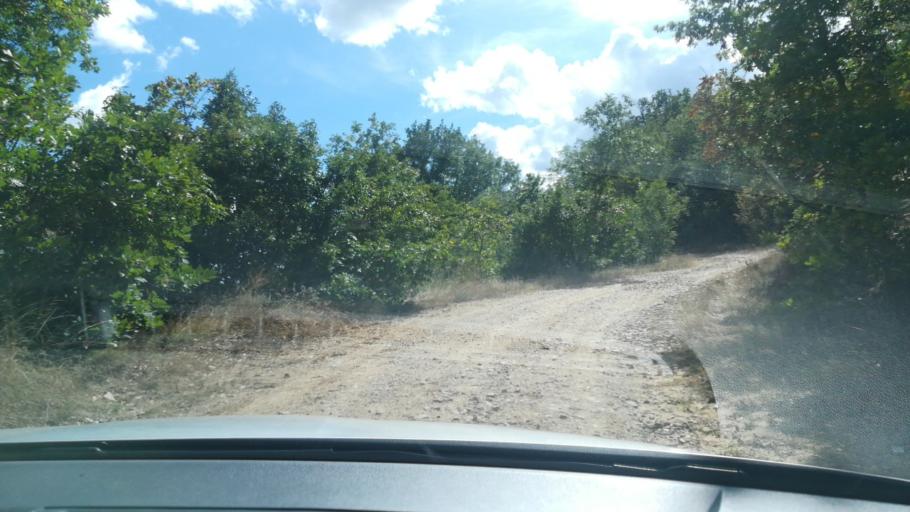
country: MK
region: Delcevo
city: Delcevo
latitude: 41.8959
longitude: 22.8059
